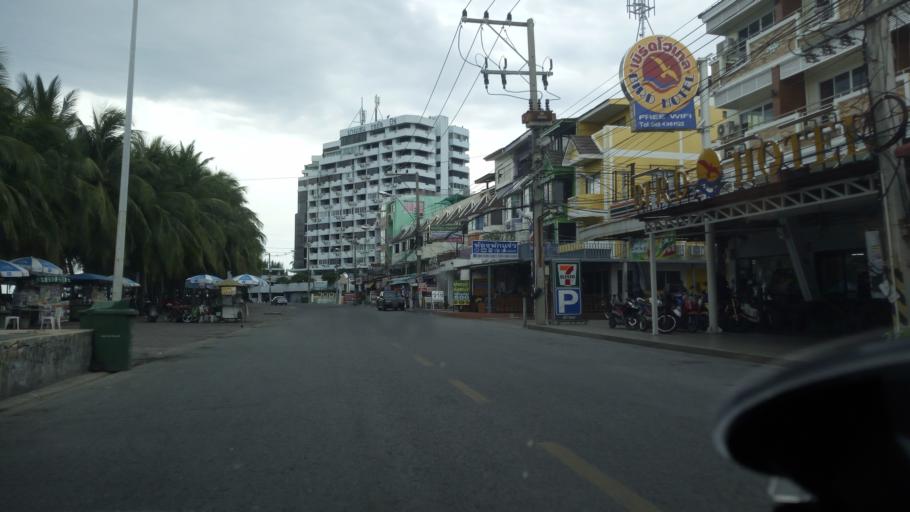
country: TH
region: Chon Buri
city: Chon Buri
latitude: 13.2995
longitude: 100.9010
